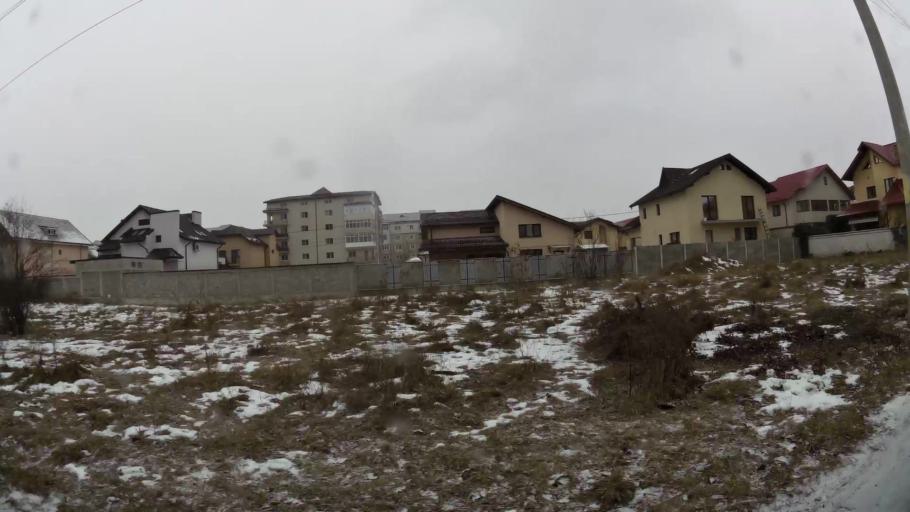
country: RO
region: Dambovita
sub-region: Municipiul Targoviste
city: Targoviste
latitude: 44.9321
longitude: 25.4442
